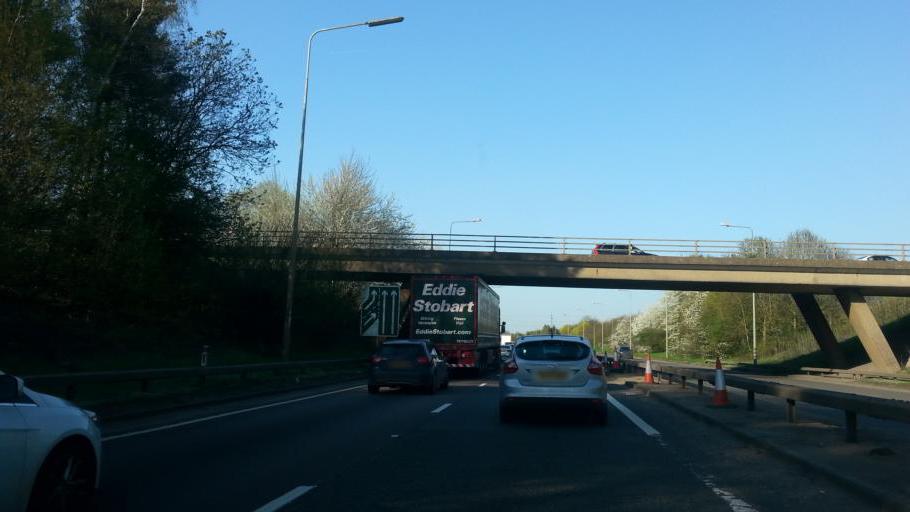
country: GB
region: England
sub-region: Northamptonshire
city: Hardingstone
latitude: 52.2215
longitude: -0.8762
